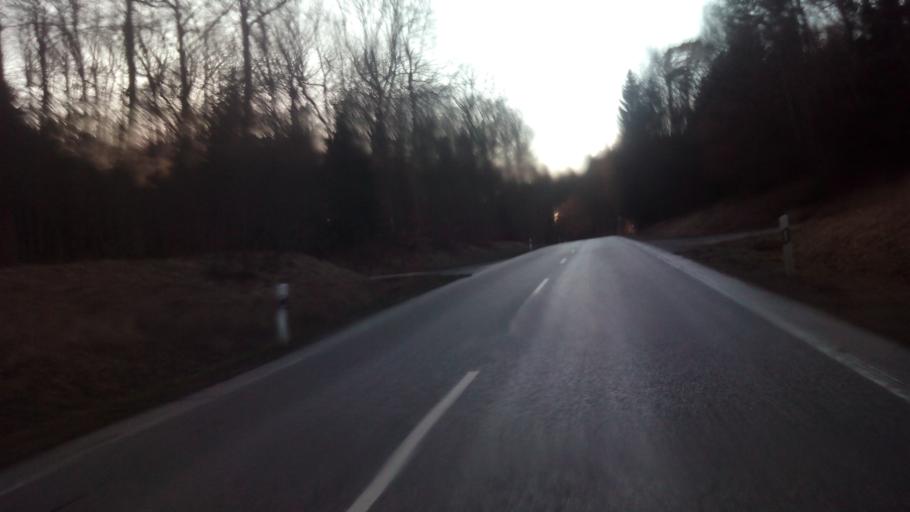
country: DE
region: Baden-Wuerttemberg
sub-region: Tuebingen Region
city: Altheim
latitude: 48.3481
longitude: 9.7955
